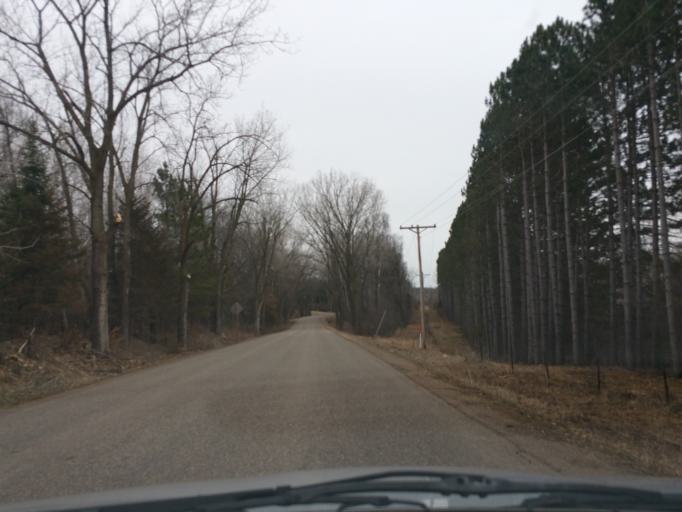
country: US
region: Wisconsin
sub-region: Saint Croix County
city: Roberts
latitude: 45.0071
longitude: -92.6239
